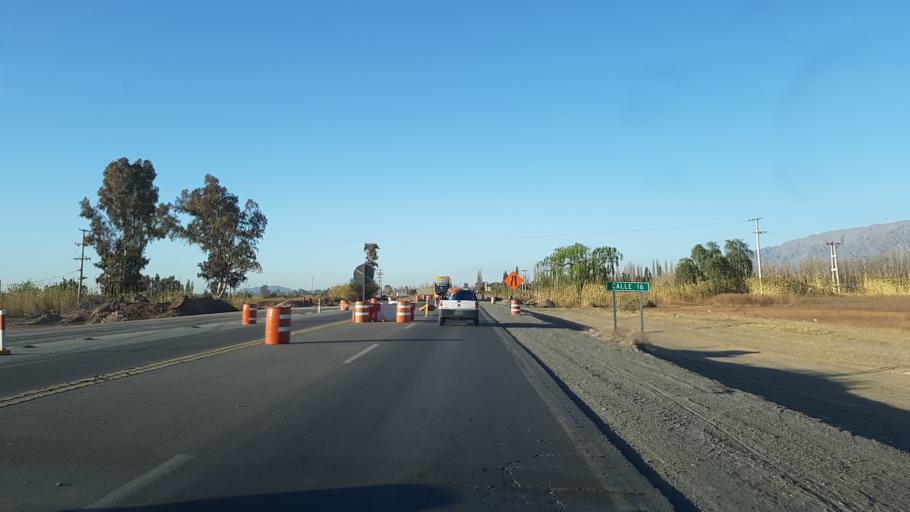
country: AR
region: San Juan
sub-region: Departamento de Pocito
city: Pocito
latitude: -31.7189
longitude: -68.5563
